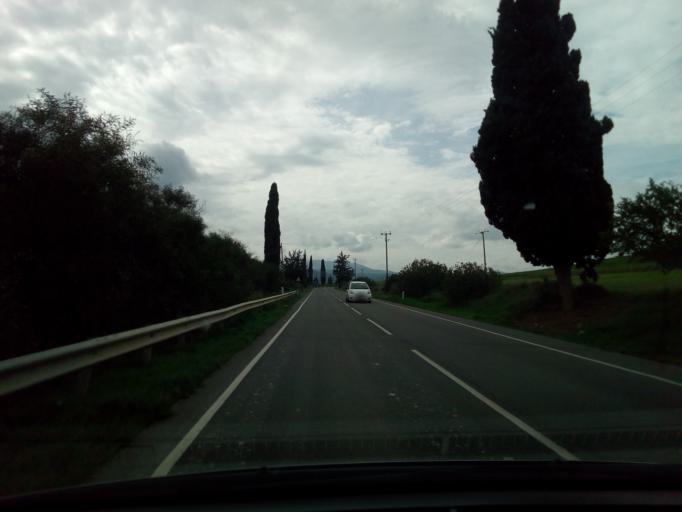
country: CY
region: Lefkosia
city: Astromeritis
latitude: 35.0914
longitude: 32.9641
